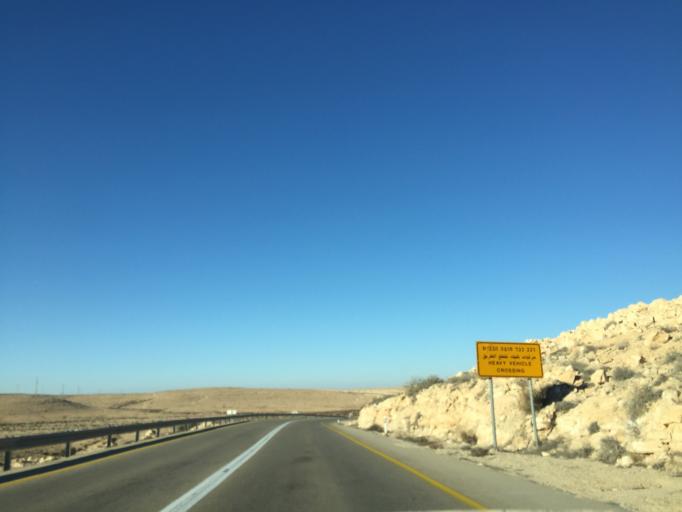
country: IL
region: Southern District
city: Mitzpe Ramon
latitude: 30.7020
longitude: 34.7836
